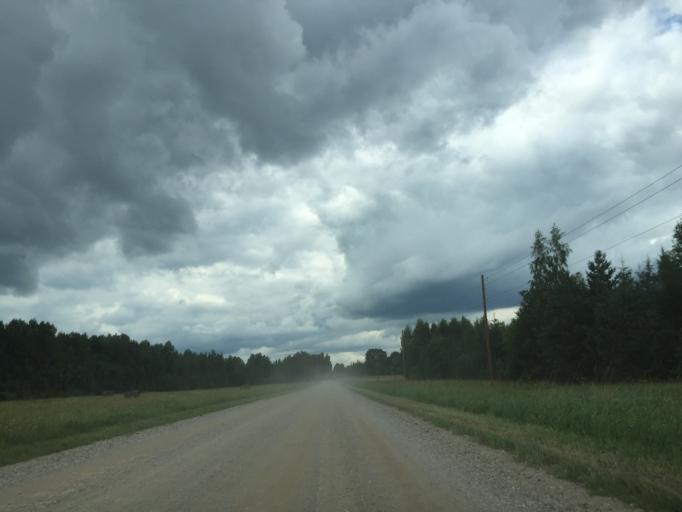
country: LV
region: Malpils
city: Malpils
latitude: 56.8680
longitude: 25.0098
